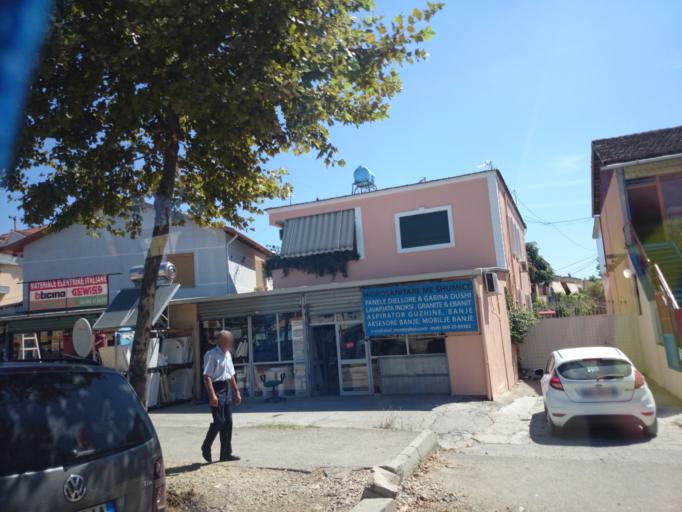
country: AL
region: Tirane
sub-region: Rrethi i Tiranes
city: Paskuqan
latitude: 41.3361
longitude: 19.7838
